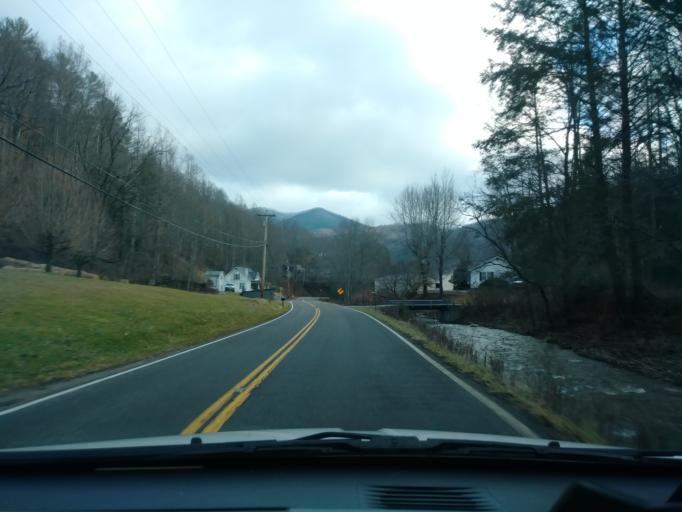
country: US
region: Tennessee
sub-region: Carter County
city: Elizabethton
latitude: 36.2248
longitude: -82.1933
